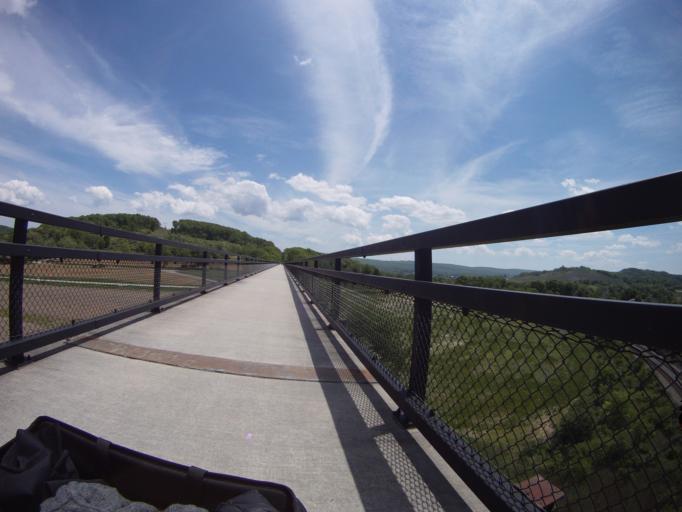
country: US
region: Pennsylvania
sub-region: Somerset County
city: Meyersdale
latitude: 39.8330
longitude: -79.0438
